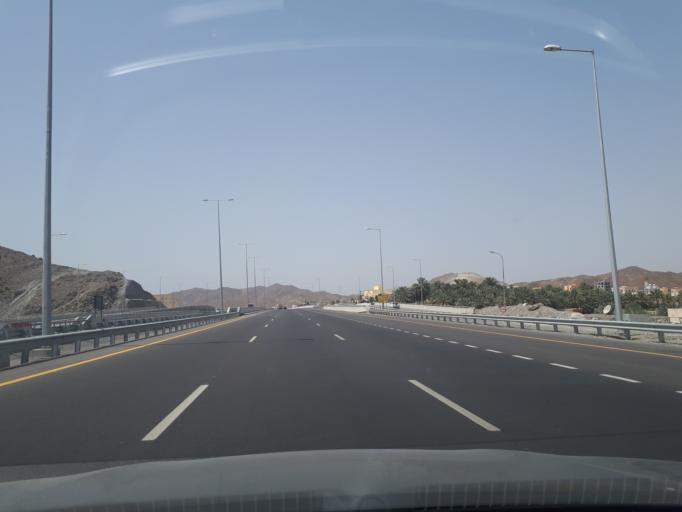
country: OM
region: Muhafazat ad Dakhiliyah
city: Bidbid
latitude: 23.4093
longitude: 58.1004
